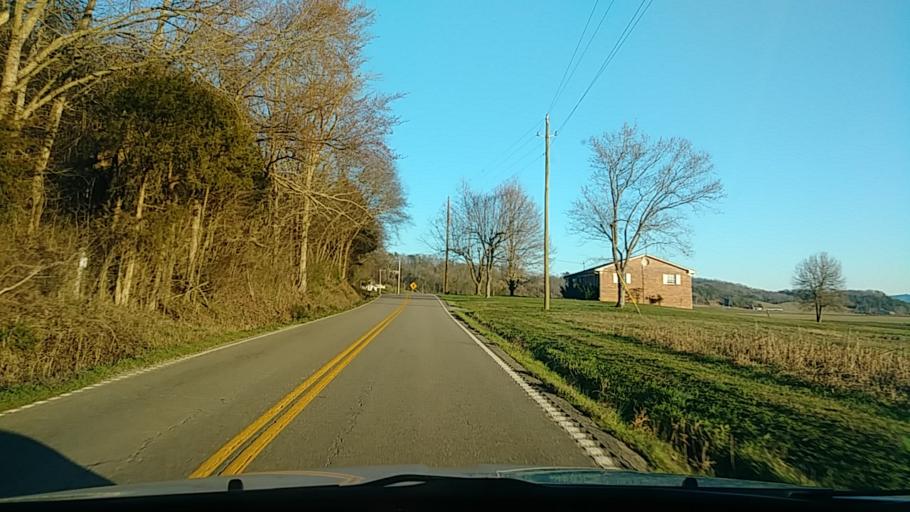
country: US
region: Tennessee
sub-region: Greene County
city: Mosheim
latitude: 36.1221
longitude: -83.0896
